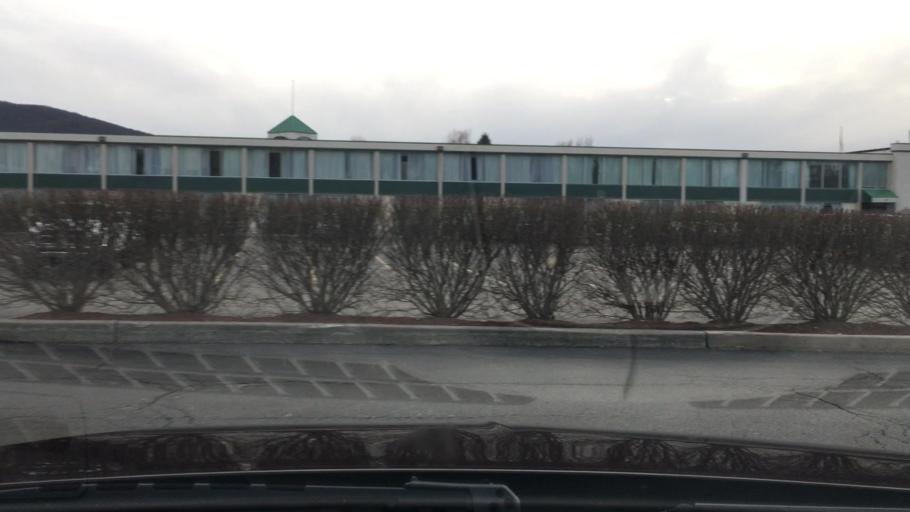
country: US
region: New York
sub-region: Dutchess County
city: Fishkill
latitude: 41.5259
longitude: -73.8882
